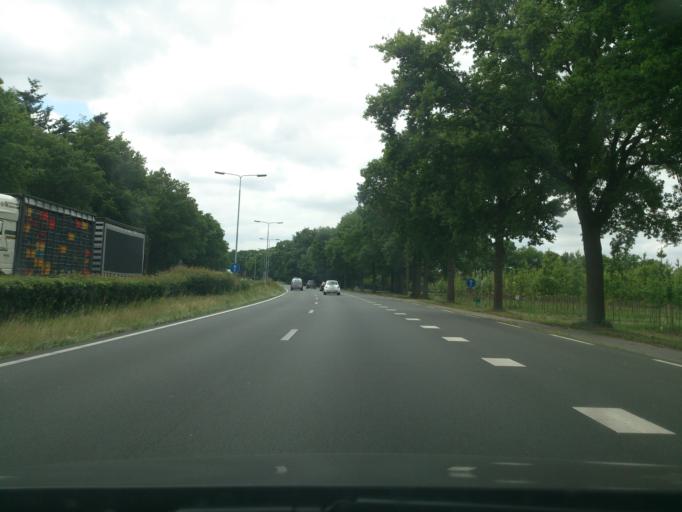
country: NL
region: North Brabant
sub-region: Gemeente Vught
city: Vught
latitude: 51.6422
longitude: 5.2550
